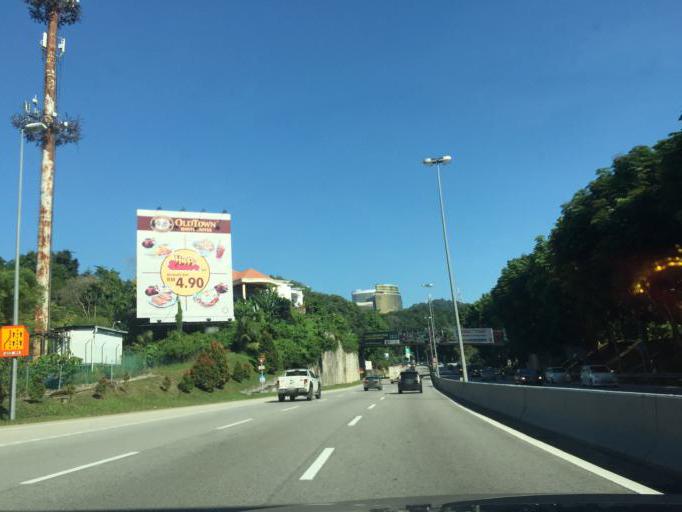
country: MY
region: Selangor
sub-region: Petaling
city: Petaling Jaya
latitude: 3.1609
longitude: 101.6234
